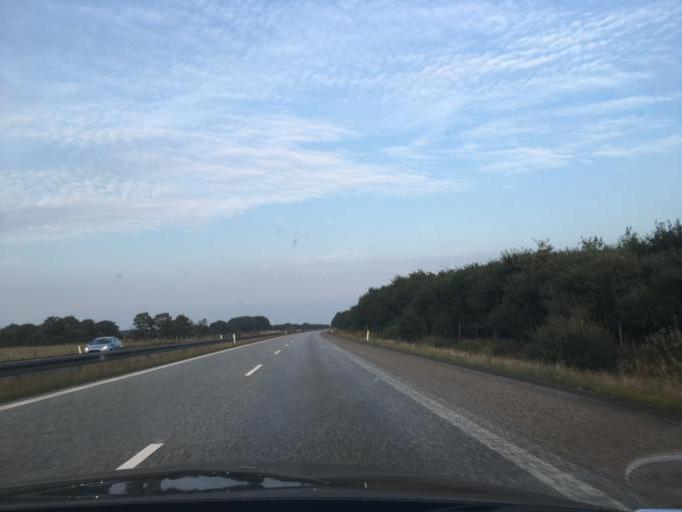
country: DK
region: South Denmark
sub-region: Esbjerg Kommune
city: Bramming
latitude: 55.5139
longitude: 8.7636
